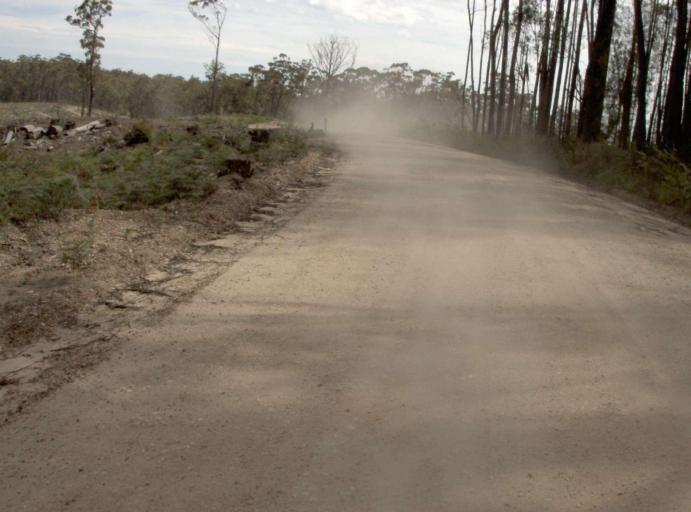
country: AU
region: Victoria
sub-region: East Gippsland
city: Lakes Entrance
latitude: -37.6370
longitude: 148.6645
